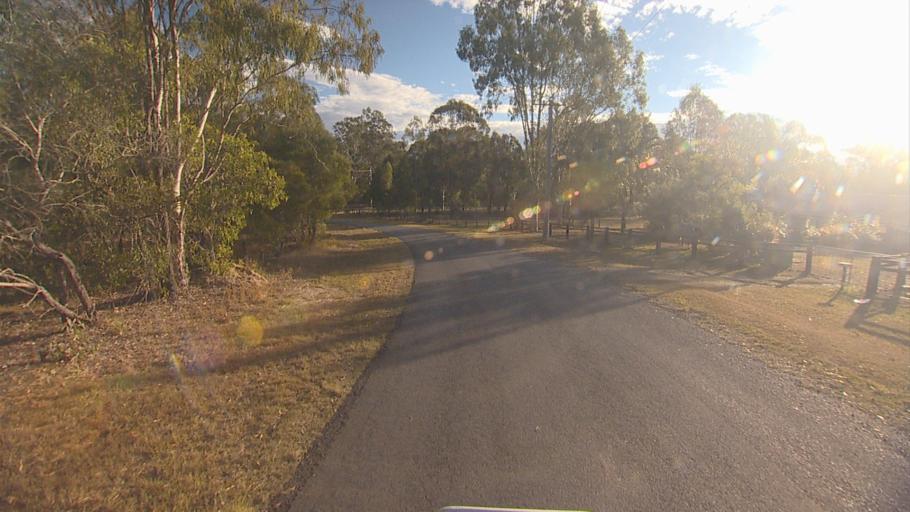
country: AU
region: Queensland
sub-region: Logan
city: Cedar Vale
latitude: -27.8616
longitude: 153.0584
